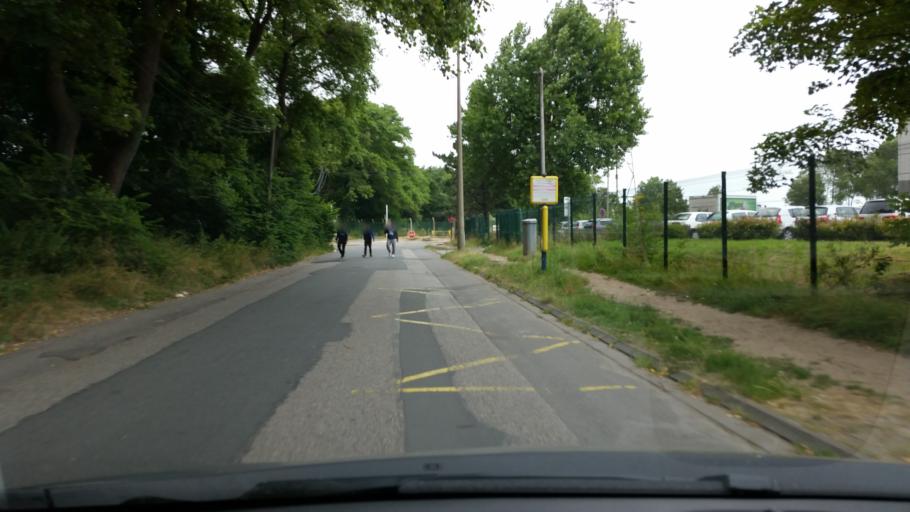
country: FR
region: Nord-Pas-de-Calais
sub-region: Departement du Pas-de-Calais
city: Calais
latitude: 50.9646
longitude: 1.8827
